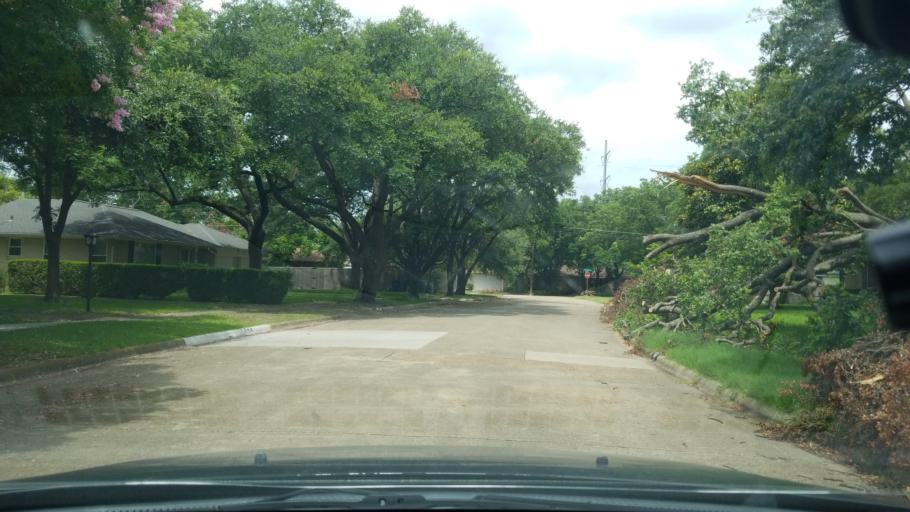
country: US
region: Texas
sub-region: Dallas County
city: Garland
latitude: 32.8295
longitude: -96.6907
